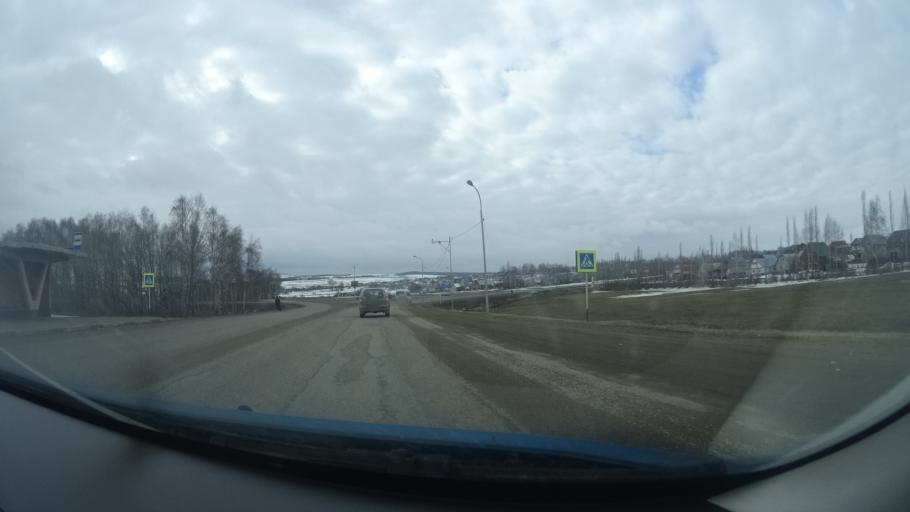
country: RU
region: Bashkortostan
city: Birsk
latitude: 55.4211
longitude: 55.5833
